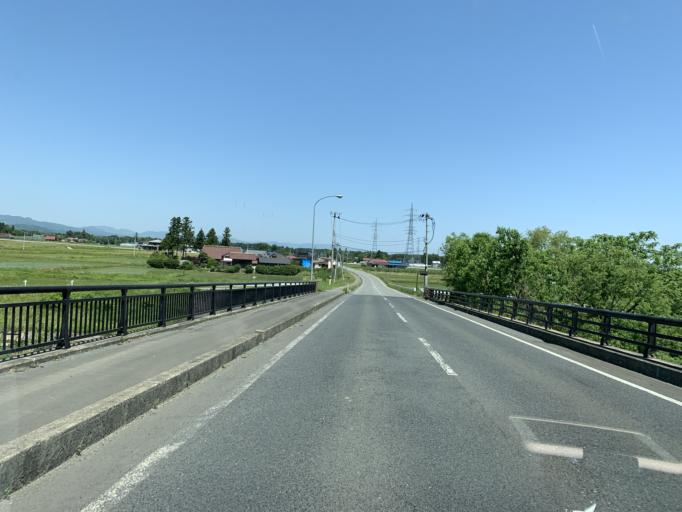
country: JP
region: Iwate
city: Mizusawa
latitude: 39.1750
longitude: 141.0819
